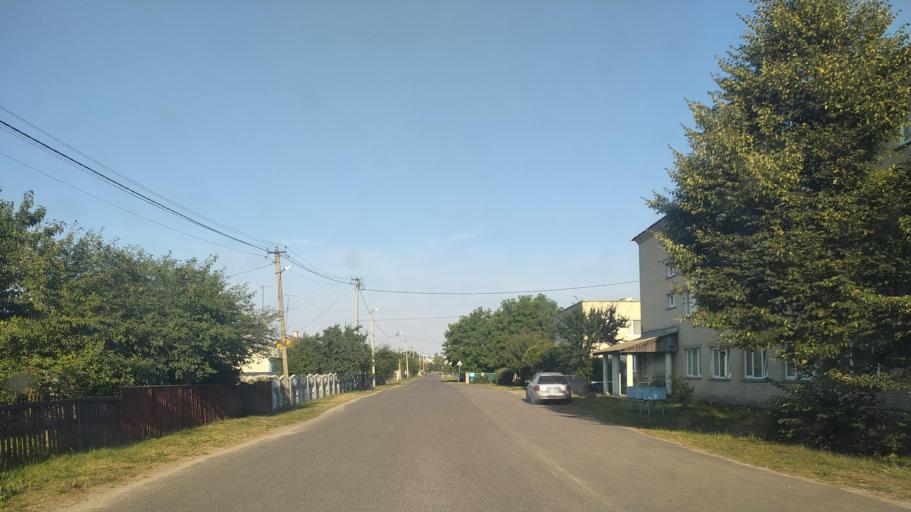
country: BY
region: Brest
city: Drahichyn
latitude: 52.1862
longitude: 25.1692
